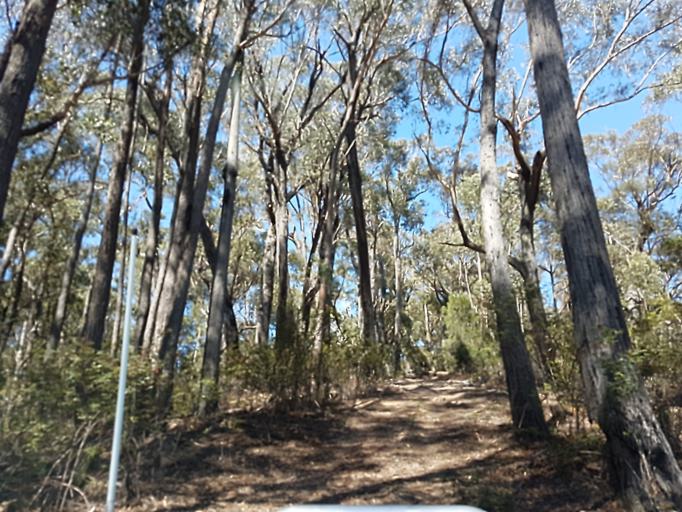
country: AU
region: Victoria
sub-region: East Gippsland
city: Lakes Entrance
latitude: -37.2887
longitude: 148.3267
